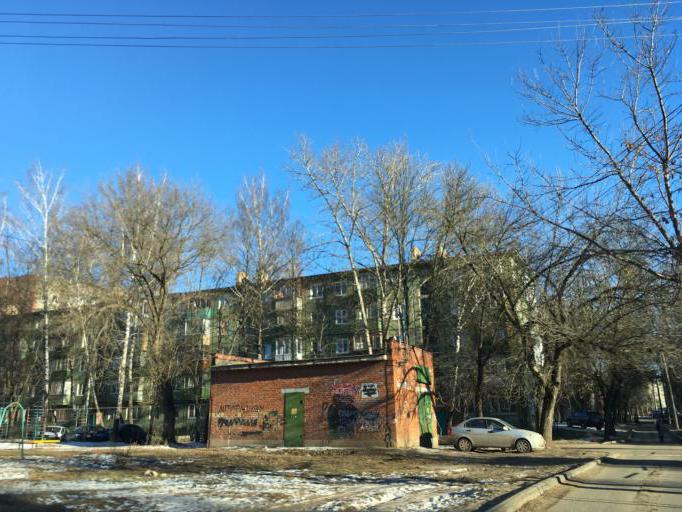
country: RU
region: Tula
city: Tula
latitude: 54.1948
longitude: 37.6769
